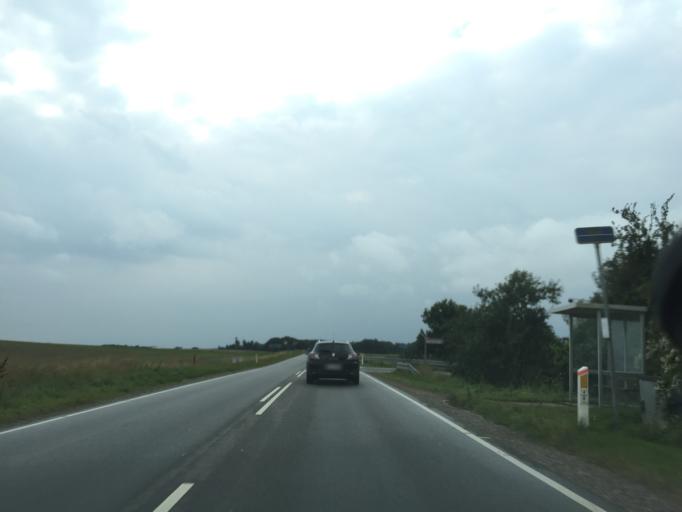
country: DK
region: Central Jutland
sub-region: Skanderborg Kommune
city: Skanderborg
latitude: 56.0656
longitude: 9.8984
